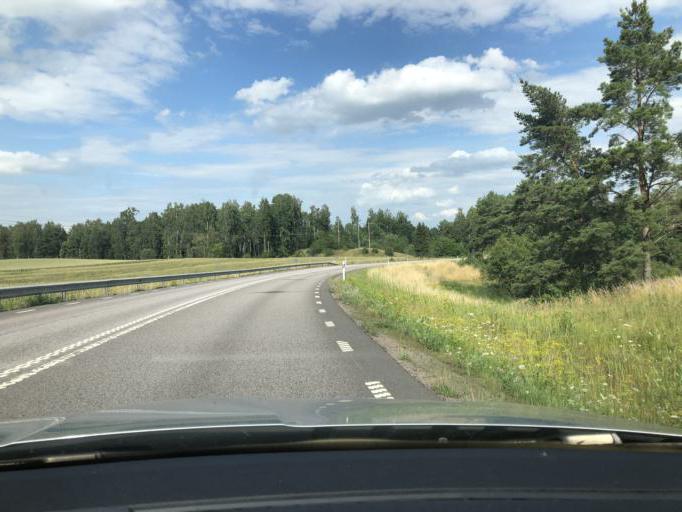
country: SE
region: OEstergoetland
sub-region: Mjolby Kommun
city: Mjolby
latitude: 58.3443
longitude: 15.1731
